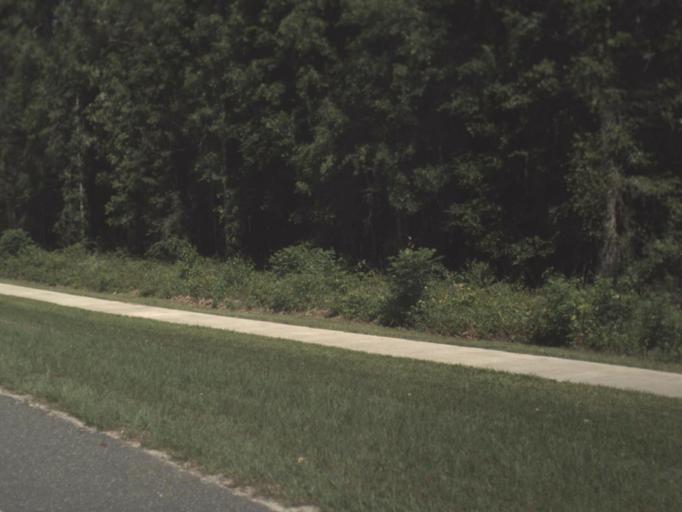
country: US
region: Florida
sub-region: Jackson County
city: Marianna
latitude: 30.8123
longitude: -85.1837
